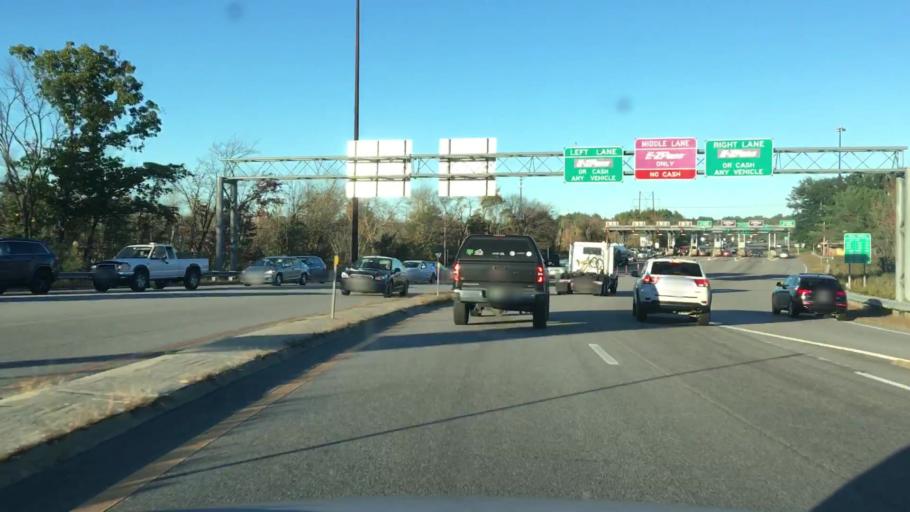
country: US
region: New Hampshire
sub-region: Rockingham County
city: North Hampton
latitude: 42.9632
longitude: -70.8627
